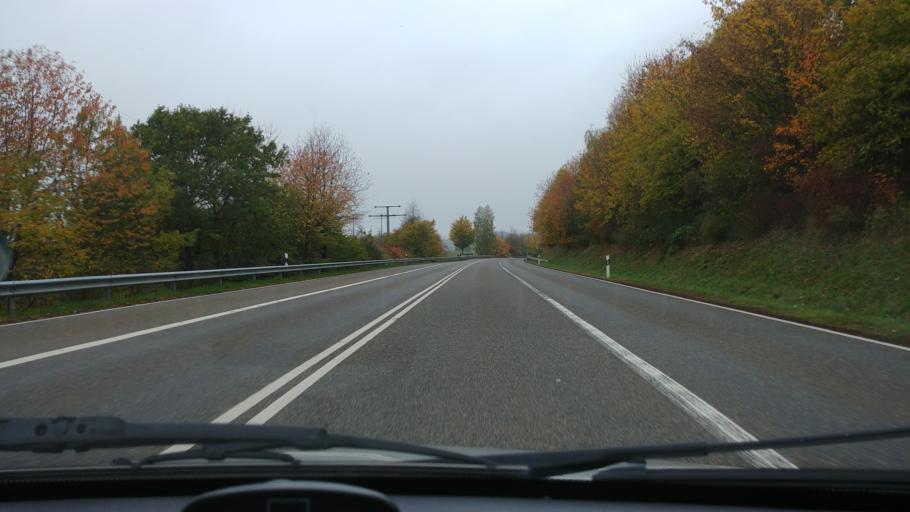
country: DE
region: Rheinland-Pfalz
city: Willmenrod
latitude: 50.5520
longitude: 7.9713
